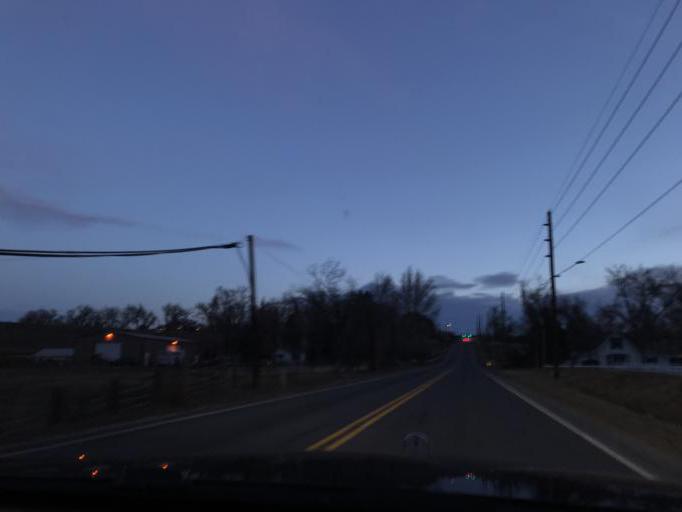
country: US
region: Colorado
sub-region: Jefferson County
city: Applewood
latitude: 39.8393
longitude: -105.1651
